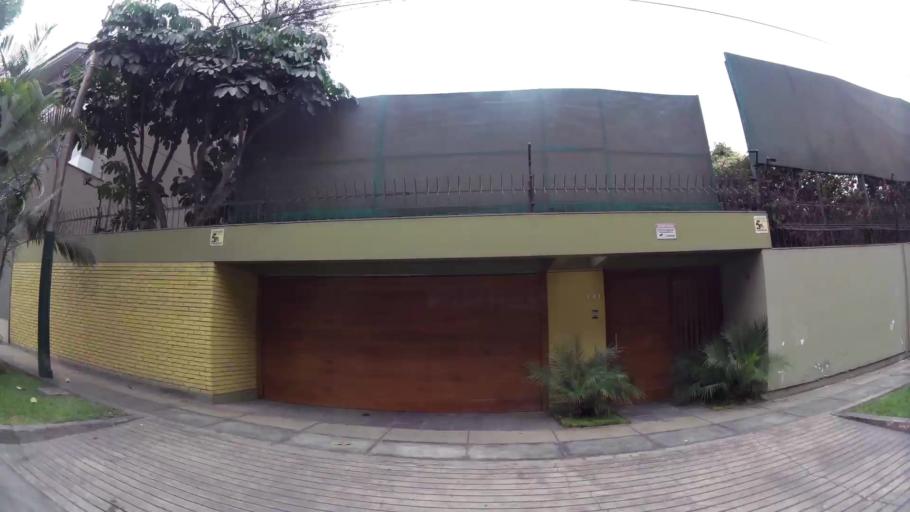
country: PE
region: Lima
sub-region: Lima
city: Surco
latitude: -12.1134
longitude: -76.9838
